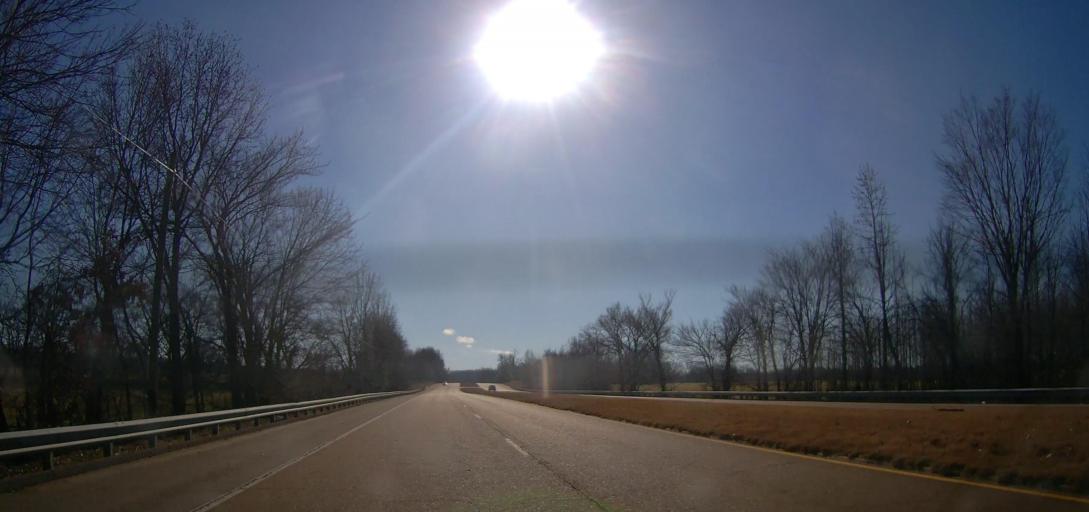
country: US
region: Tennessee
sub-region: Shelby County
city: Bartlett
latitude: 35.2704
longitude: -89.8878
